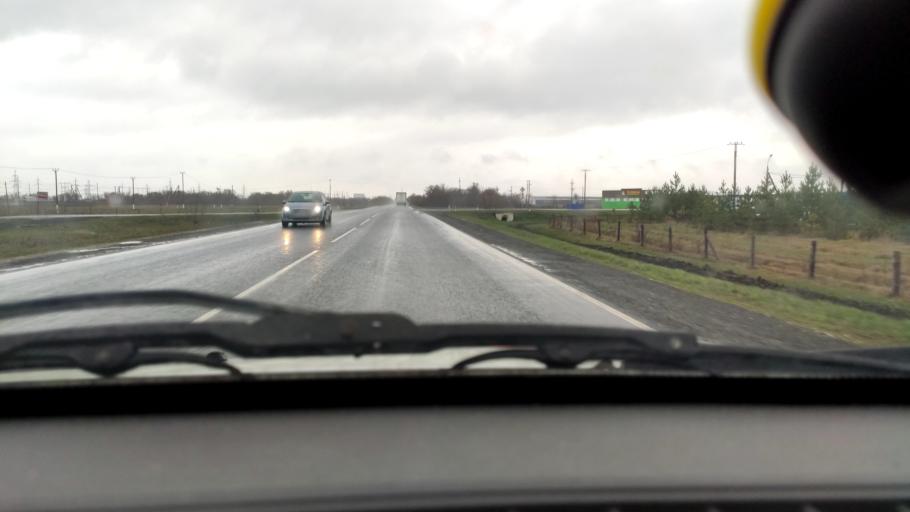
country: RU
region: Samara
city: Povolzhskiy
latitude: 53.6471
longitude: 49.6761
